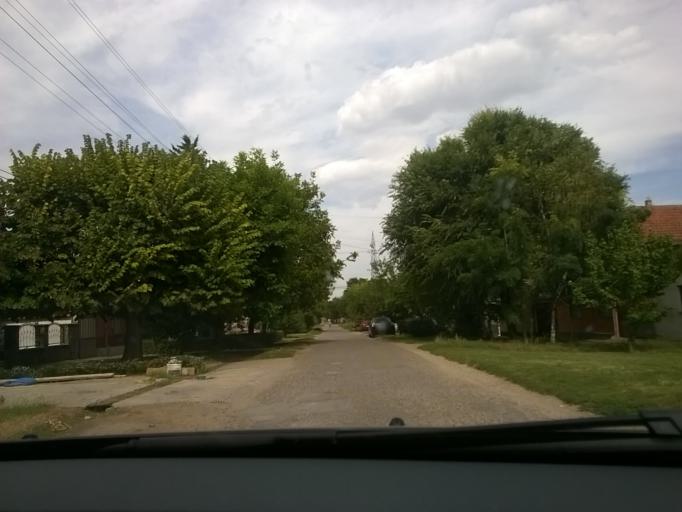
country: RS
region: Autonomna Pokrajina Vojvodina
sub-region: Juznobanatski Okrug
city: Vrsac
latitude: 45.1232
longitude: 21.2816
